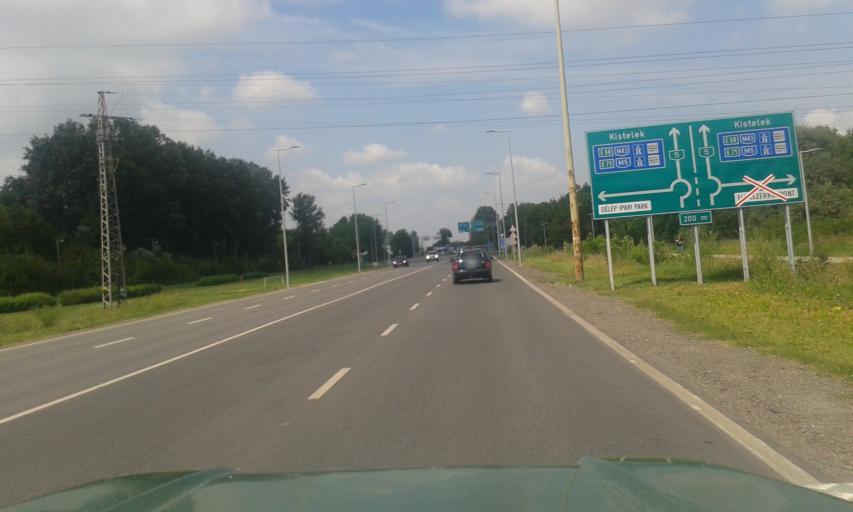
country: HU
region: Csongrad
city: Szeged
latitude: 46.2744
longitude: 20.1004
